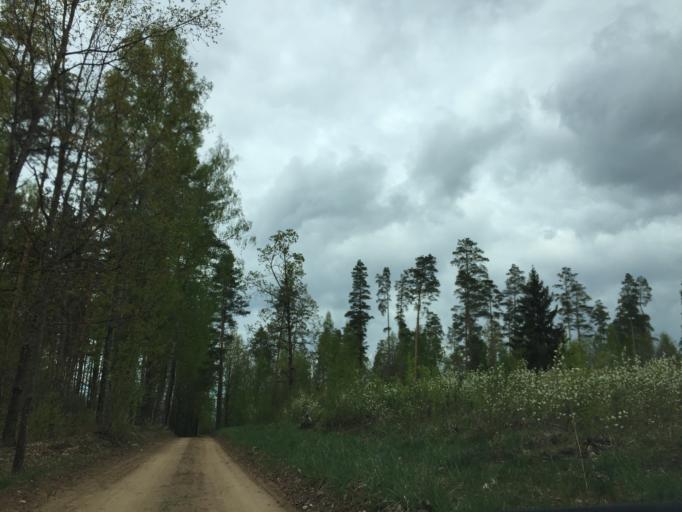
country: LV
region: Kekava
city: Kekava
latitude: 56.8031
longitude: 24.2989
